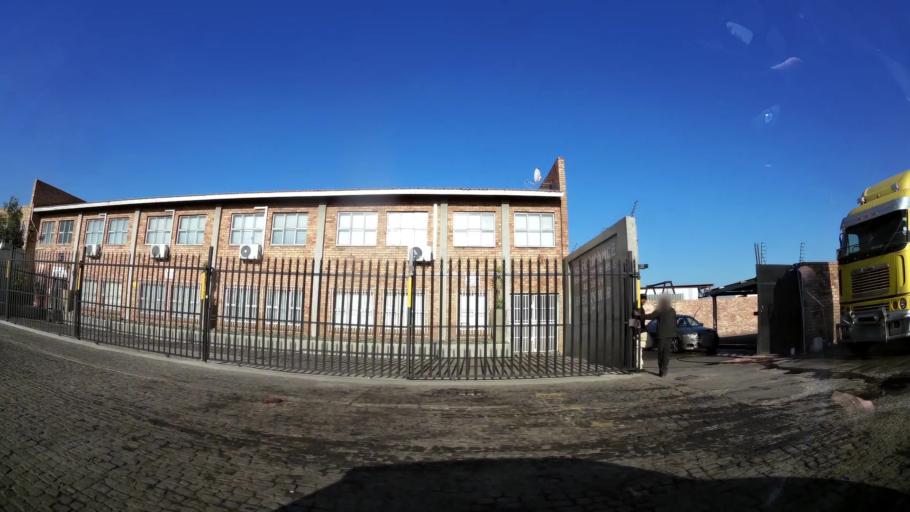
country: ZA
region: Gauteng
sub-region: West Rand District Municipality
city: Randfontein
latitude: -26.1950
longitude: 27.6909
